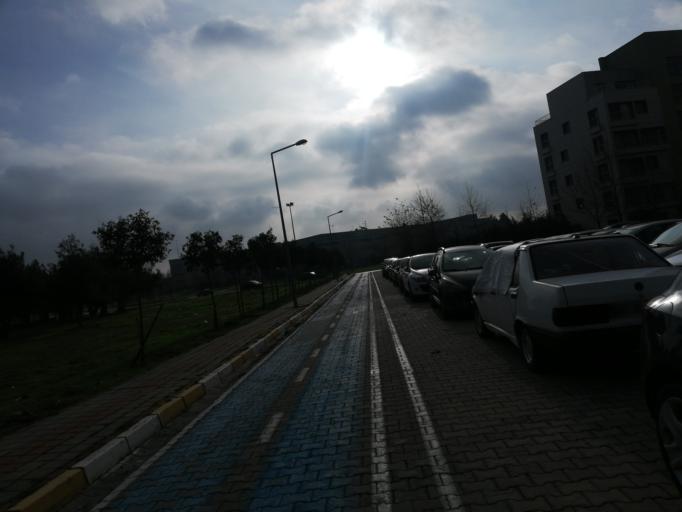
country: TR
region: Istanbul
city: merter keresteciler
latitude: 41.0303
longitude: 28.8887
